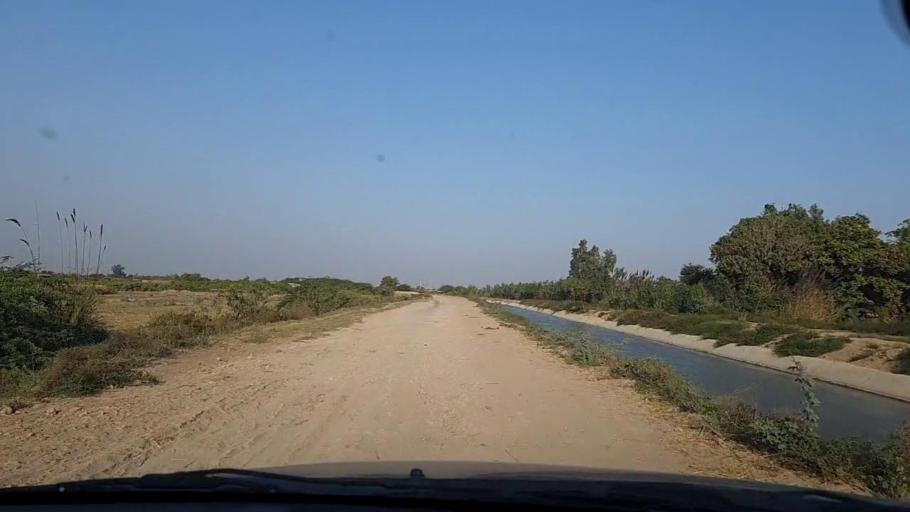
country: PK
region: Sindh
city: Chuhar Jamali
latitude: 24.2884
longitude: 67.7517
